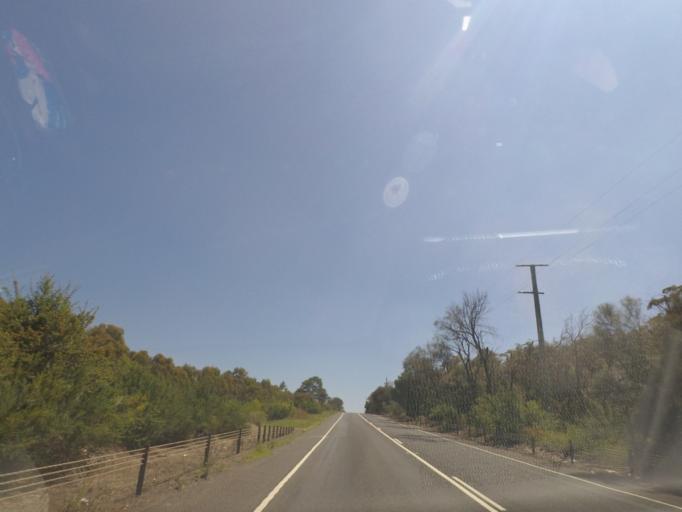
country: AU
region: Victoria
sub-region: Hume
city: Greenvale
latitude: -37.6095
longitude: 144.8400
